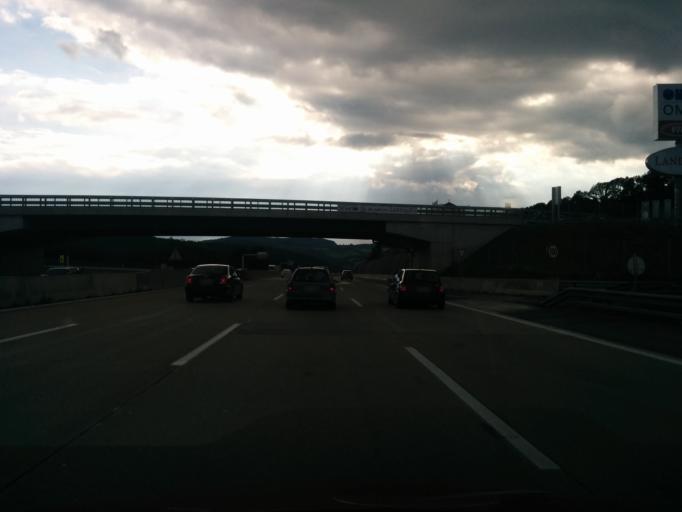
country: AT
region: Lower Austria
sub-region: Politischer Bezirk Sankt Polten
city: Altlengbach
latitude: 48.1575
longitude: 15.9445
